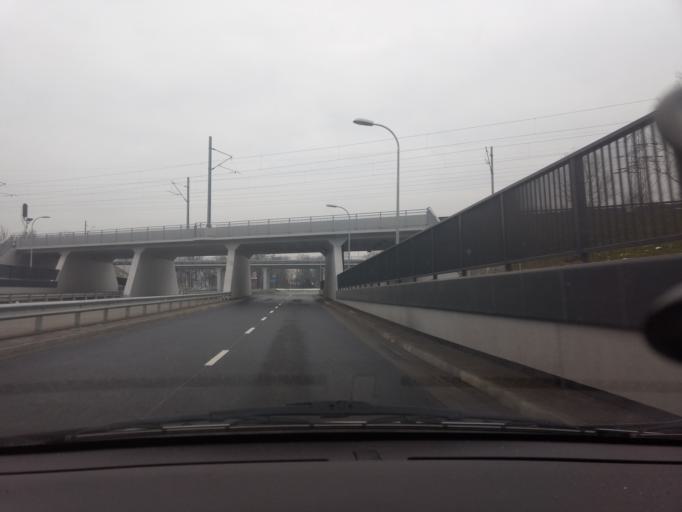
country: PL
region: Masovian Voivodeship
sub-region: Warszawa
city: Praga Poludnie
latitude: 52.2602
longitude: 21.0643
